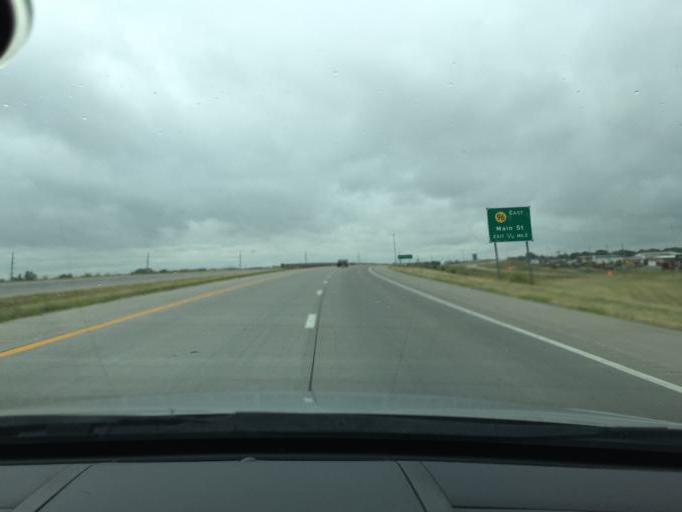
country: US
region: Kansas
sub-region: Reno County
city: South Hutchinson
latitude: 38.0134
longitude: -97.9195
